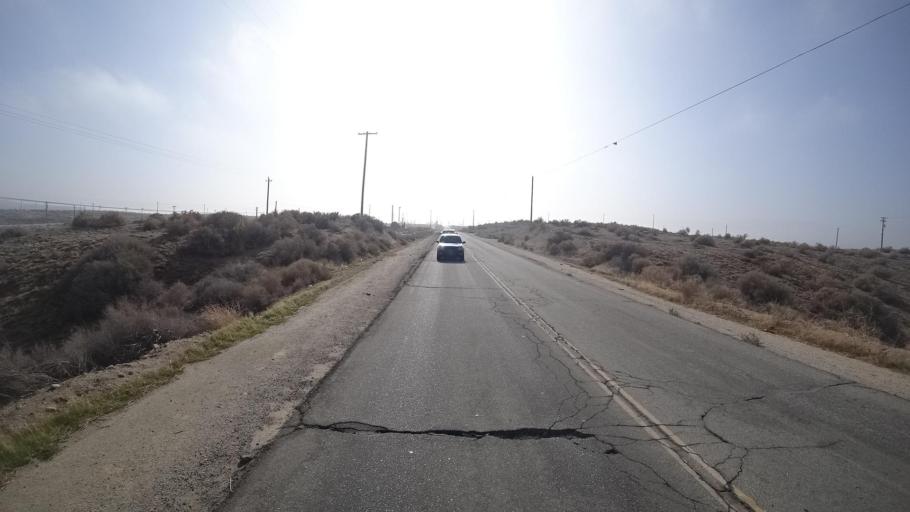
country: US
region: California
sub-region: Kern County
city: Ford City
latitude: 35.1771
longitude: -119.4657
